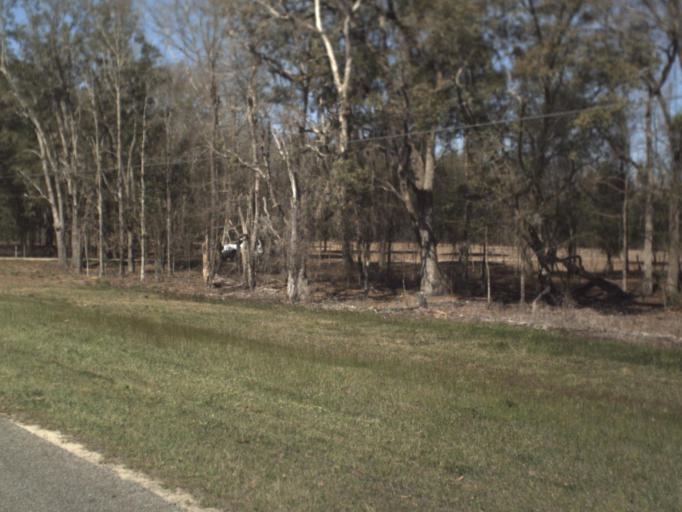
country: US
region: Florida
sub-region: Jackson County
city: Sneads
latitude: 30.7189
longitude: -84.9874
